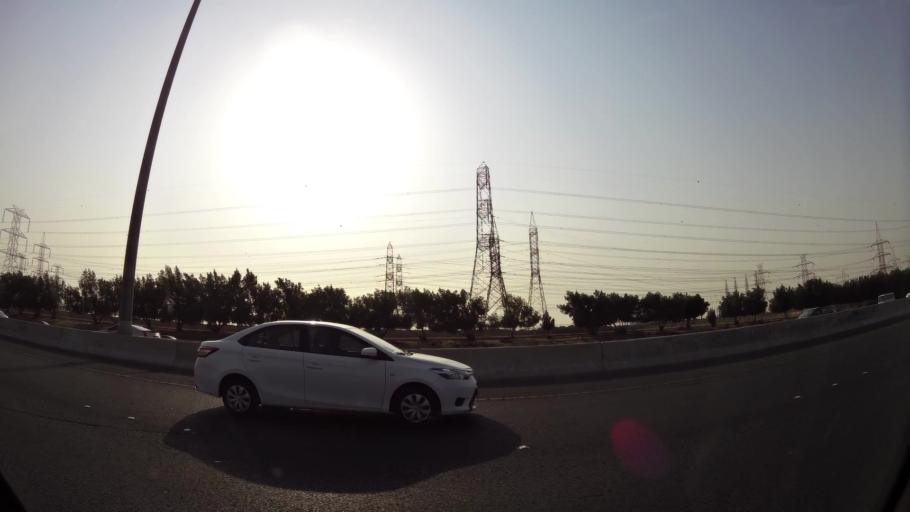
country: KW
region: Mubarak al Kabir
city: Sabah as Salim
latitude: 29.2588
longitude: 48.0445
